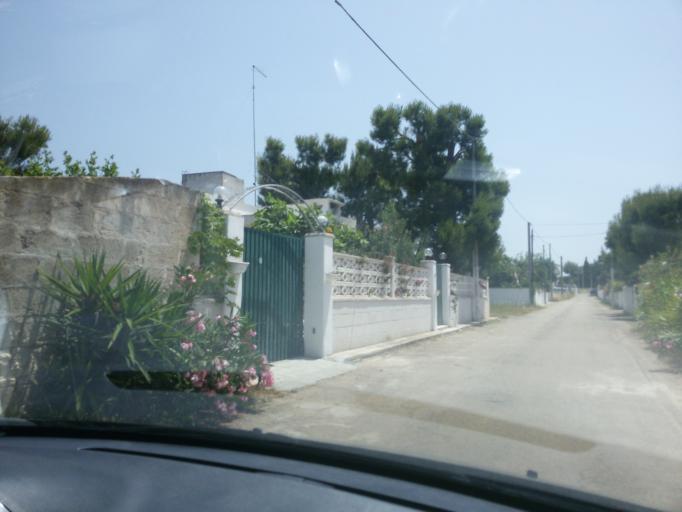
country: IT
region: Apulia
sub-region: Provincia di Lecce
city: Porto Cesareo
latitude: 40.2532
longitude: 17.9192
